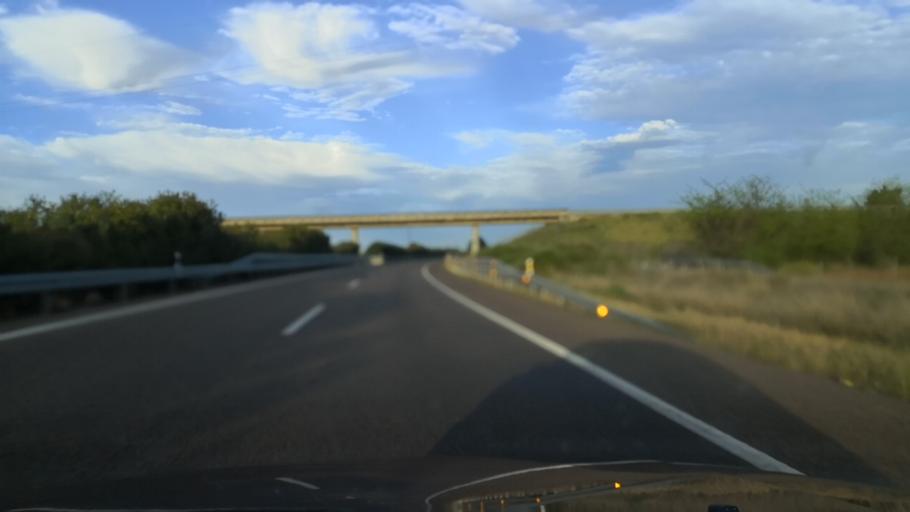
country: ES
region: Extremadura
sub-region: Provincia de Badajoz
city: Torremayor
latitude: 38.8672
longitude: -6.5054
